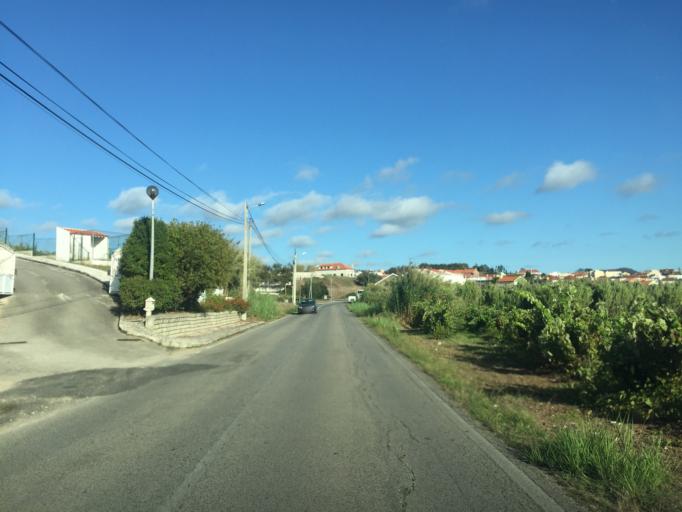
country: PT
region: Lisbon
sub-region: Torres Vedras
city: A dos Cunhados
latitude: 39.1576
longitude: -9.3020
